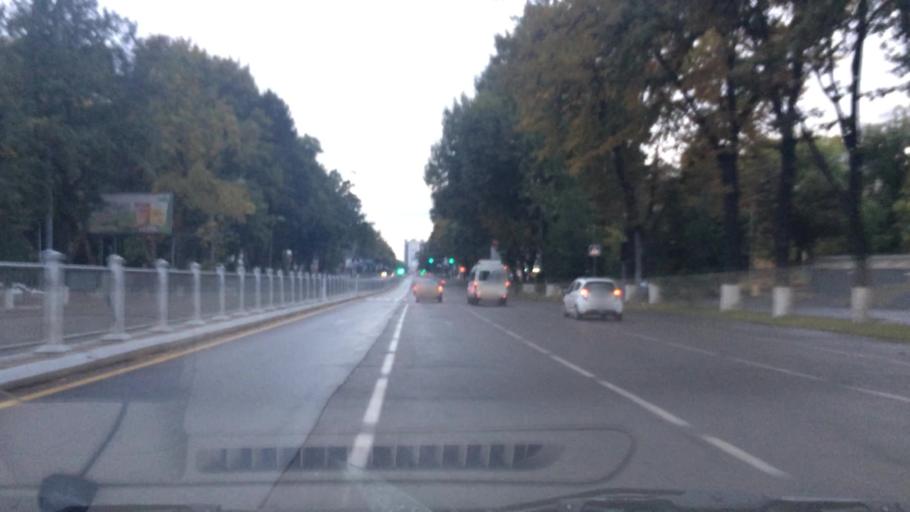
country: UZ
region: Toshkent Shahri
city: Tashkent
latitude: 41.3210
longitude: 69.2580
